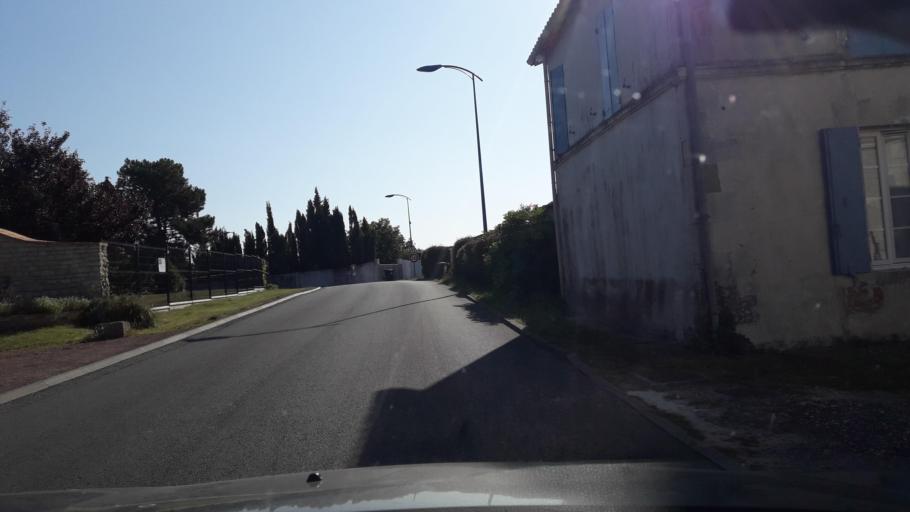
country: FR
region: Poitou-Charentes
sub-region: Departement de la Charente-Maritime
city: Etaules
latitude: 45.7156
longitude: -1.1091
